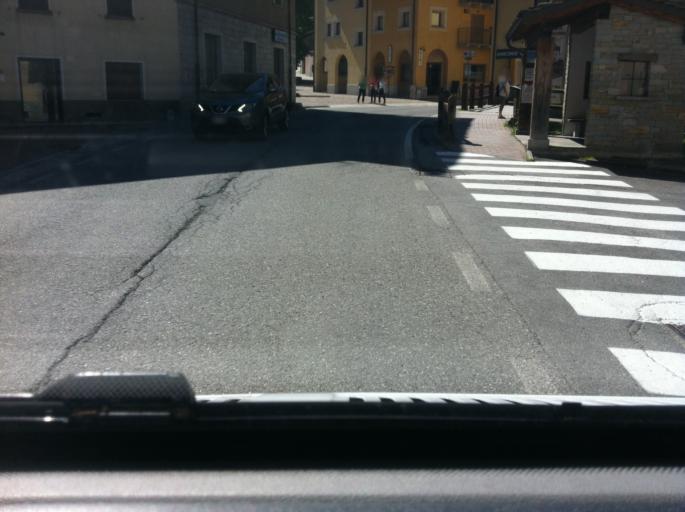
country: IT
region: Lombardy
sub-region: Provincia di Sondrio
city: Campodolcino
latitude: 46.4206
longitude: 9.3410
